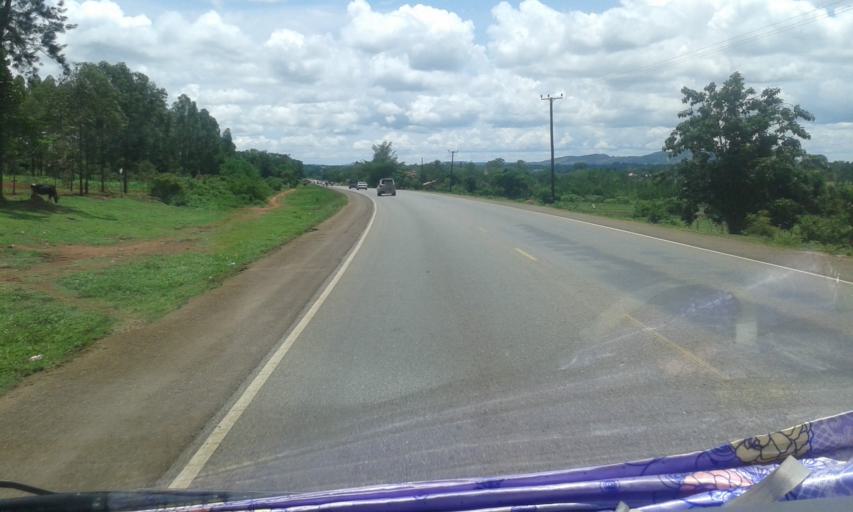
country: UG
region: Eastern Region
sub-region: Iganga District
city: Iganga
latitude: 0.5937
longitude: 33.4491
